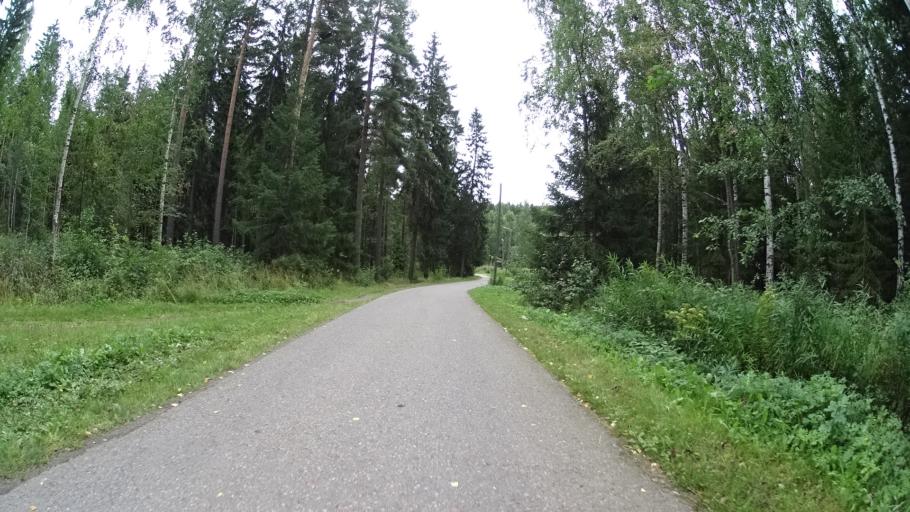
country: FI
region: Uusimaa
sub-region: Helsinki
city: Kilo
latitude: 60.2764
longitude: 24.8249
